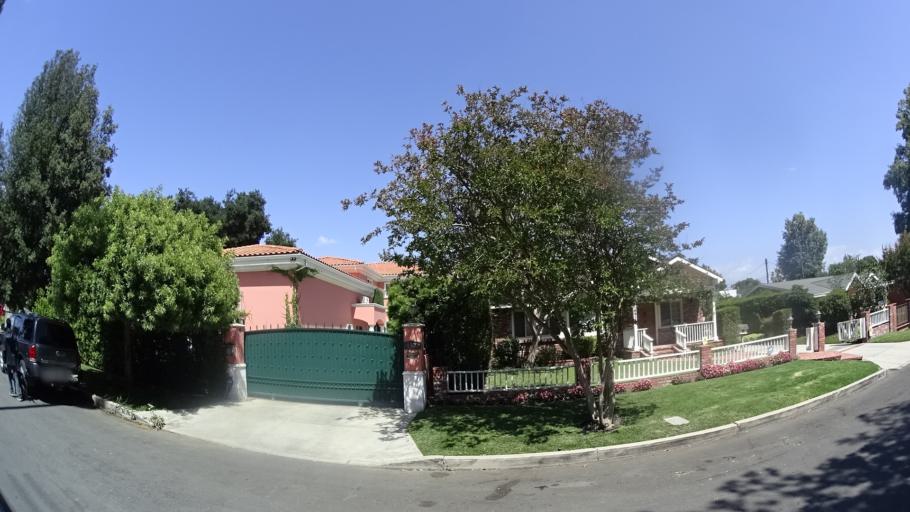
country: US
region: California
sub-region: Los Angeles County
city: Sherman Oaks
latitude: 34.1537
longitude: -118.4341
